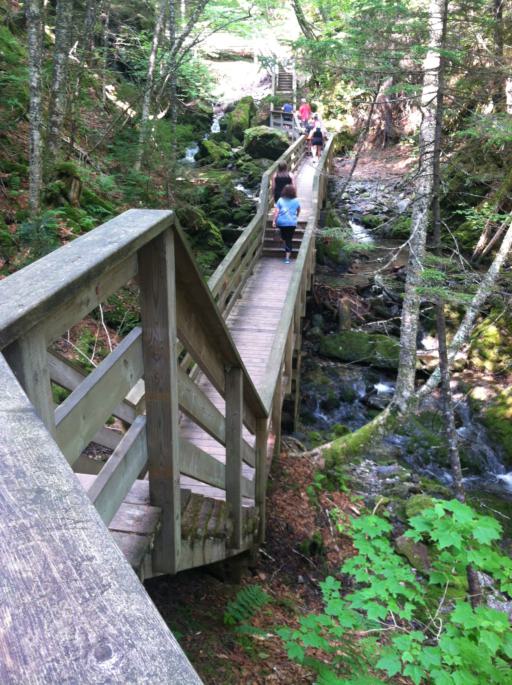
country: CA
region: New Brunswick
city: Salisbury
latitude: 45.5857
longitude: -64.9719
